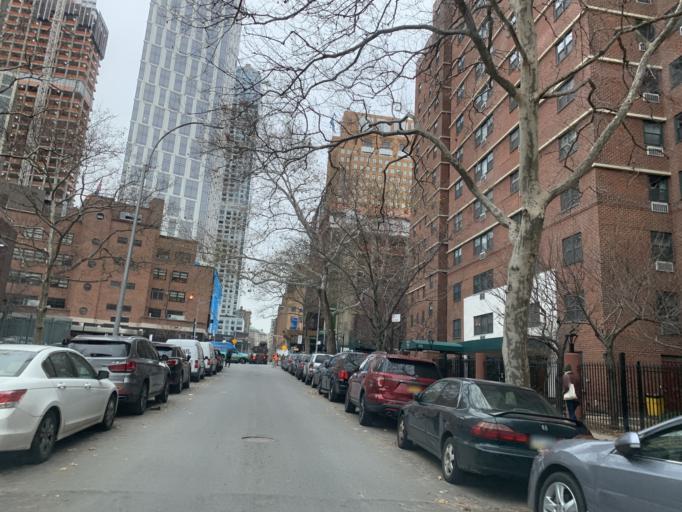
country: US
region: New York
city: New York City
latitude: 40.6920
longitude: -73.9810
